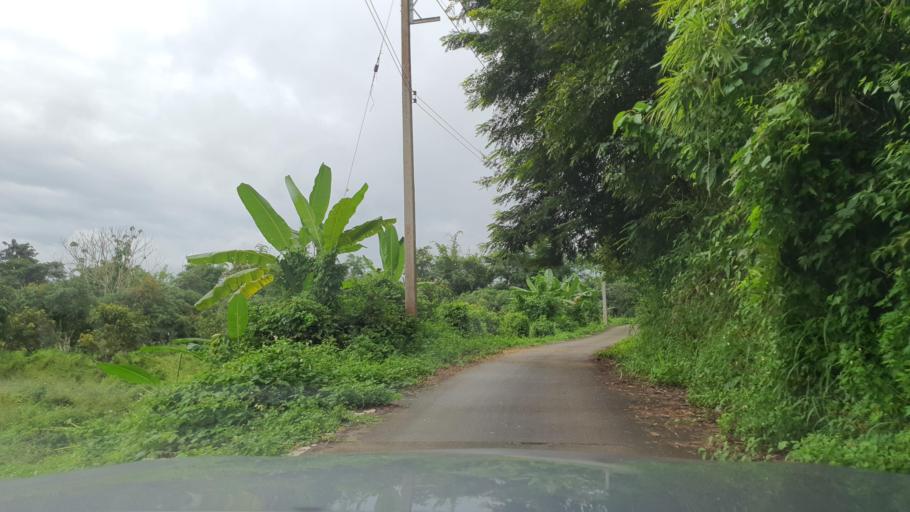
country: TH
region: Chiang Mai
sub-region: Amphoe Chiang Dao
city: Chiang Dao
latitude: 19.3363
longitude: 98.9275
